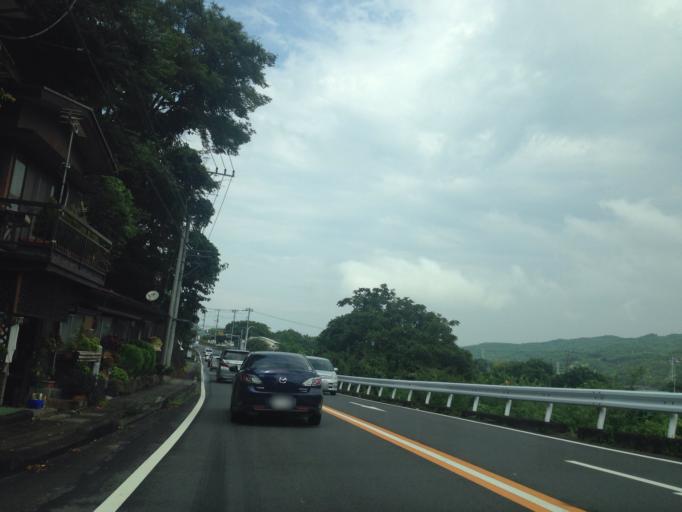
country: JP
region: Shizuoka
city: Heda
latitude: 34.9475
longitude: 138.9345
